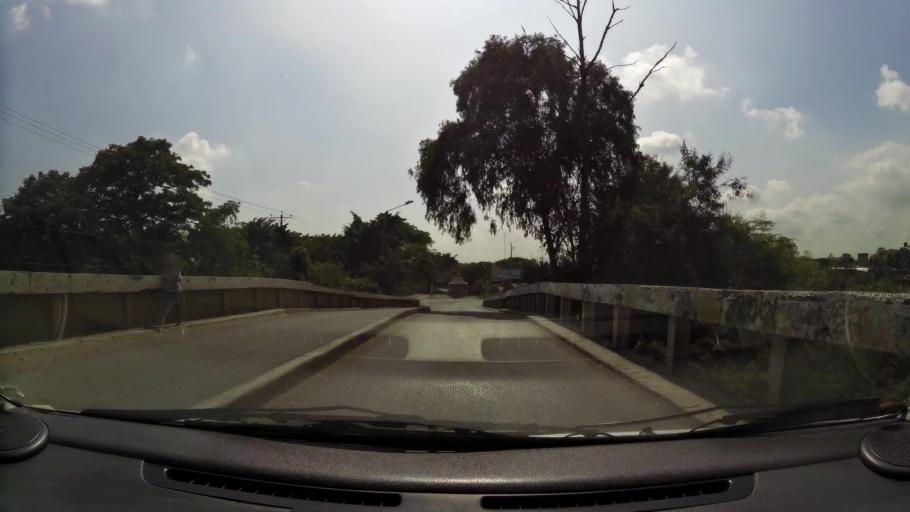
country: EC
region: Guayas
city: Eloy Alfaro
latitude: -2.1527
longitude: -79.8343
